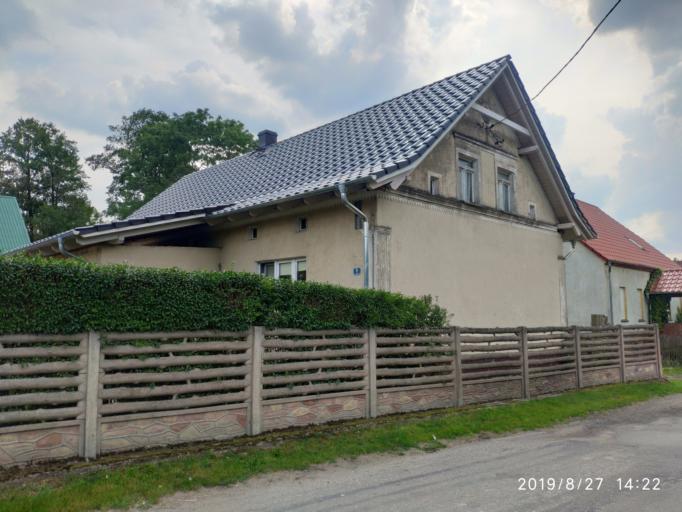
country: PL
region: Lubusz
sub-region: Powiat krosnienski
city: Bobrowice
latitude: 51.9827
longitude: 15.1089
